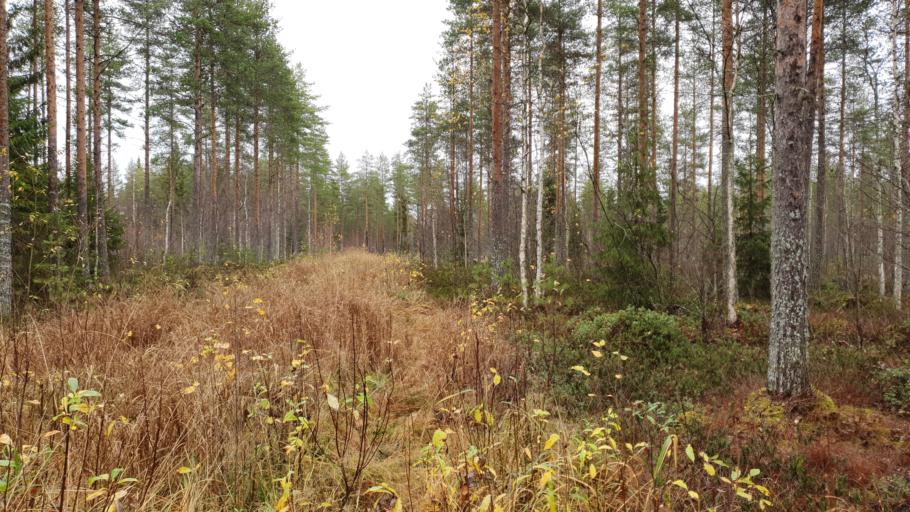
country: FI
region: Kainuu
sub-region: Kehys-Kainuu
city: Kuhmo
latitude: 64.1420
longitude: 29.4189
